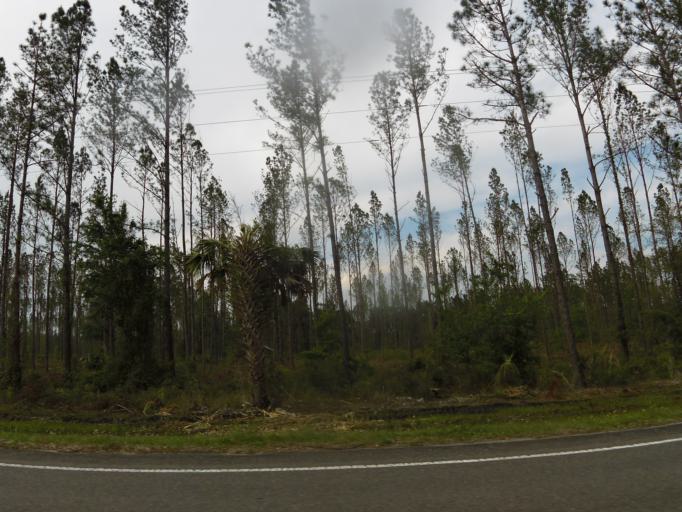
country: US
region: Florida
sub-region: Nassau County
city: Hilliard
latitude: 30.6949
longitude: -81.8158
